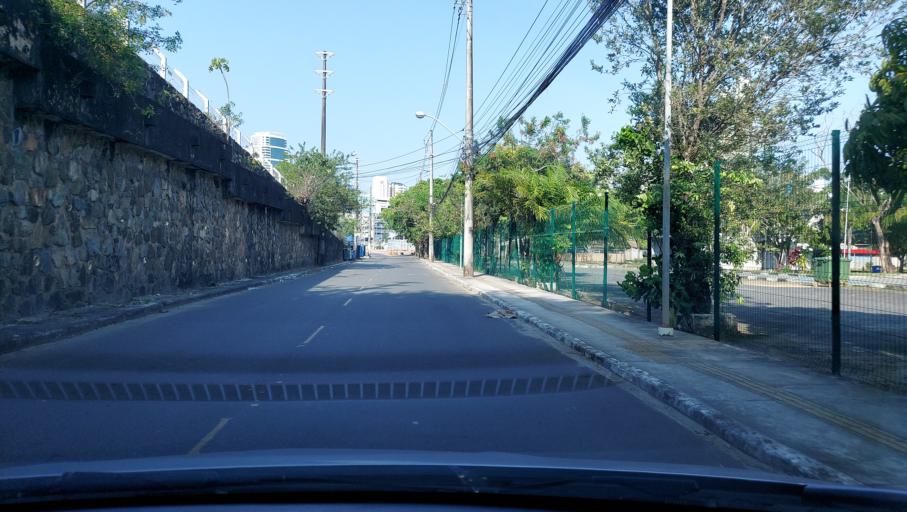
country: BR
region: Bahia
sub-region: Salvador
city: Salvador
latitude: -12.9834
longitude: -38.4685
